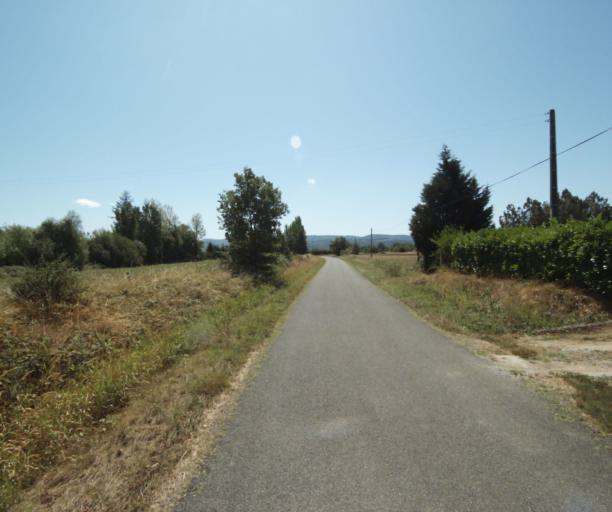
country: FR
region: Midi-Pyrenees
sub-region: Departement de la Haute-Garonne
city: Revel
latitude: 43.4769
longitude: 1.9782
